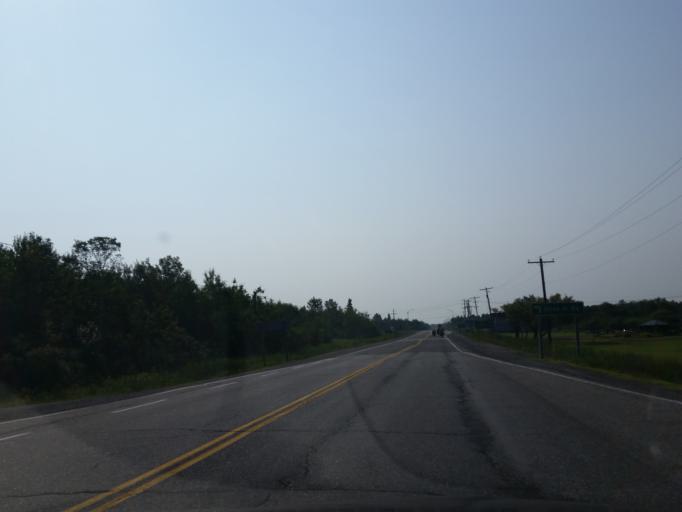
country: CA
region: Ontario
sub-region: Nipissing District
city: North Bay
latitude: 46.3798
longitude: -79.9775
